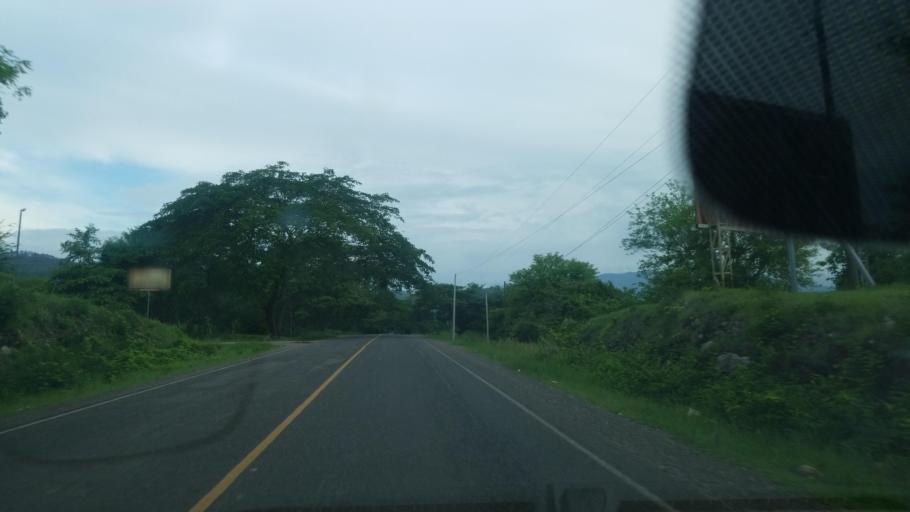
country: HN
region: Santa Barbara
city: Santa Barbara
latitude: 14.8881
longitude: -88.2486
